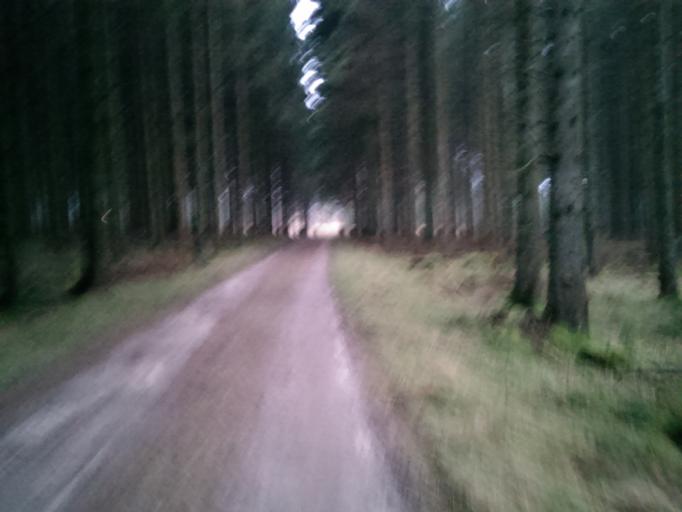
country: DK
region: North Denmark
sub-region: Mariagerfjord Kommune
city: Arden
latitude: 56.7943
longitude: 9.7574
